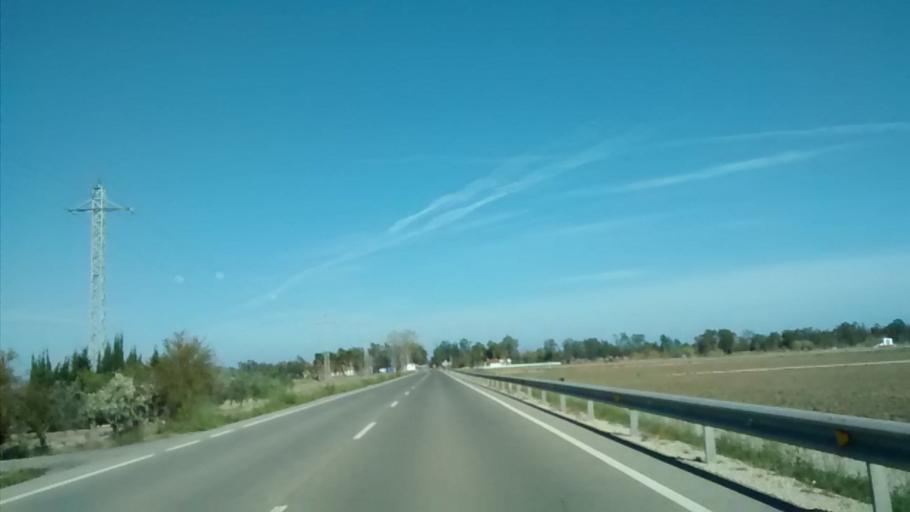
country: ES
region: Catalonia
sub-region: Provincia de Tarragona
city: Deltebre
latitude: 40.7127
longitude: 0.8220
